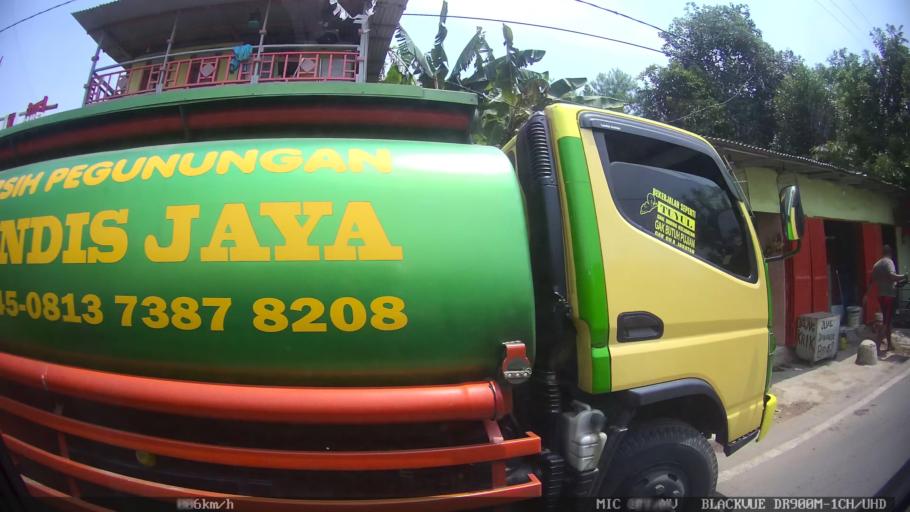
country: ID
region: Lampung
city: Bandarlampung
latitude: -5.4527
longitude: 105.2537
